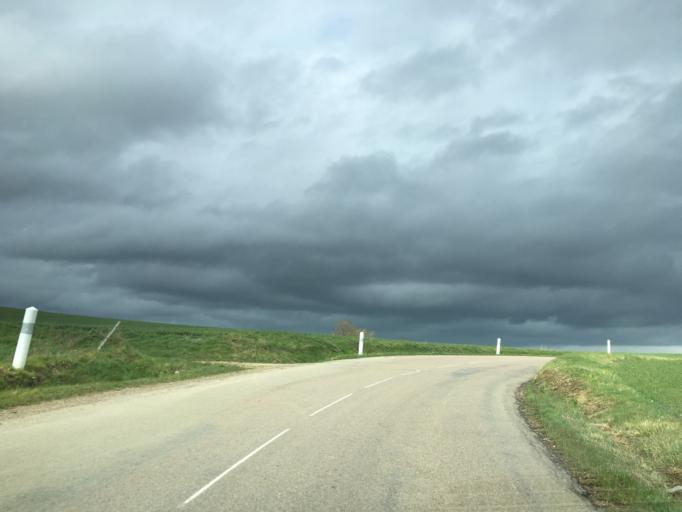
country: FR
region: Bourgogne
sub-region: Departement de l'Yonne
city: Pourrain
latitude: 47.7962
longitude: 3.4091
